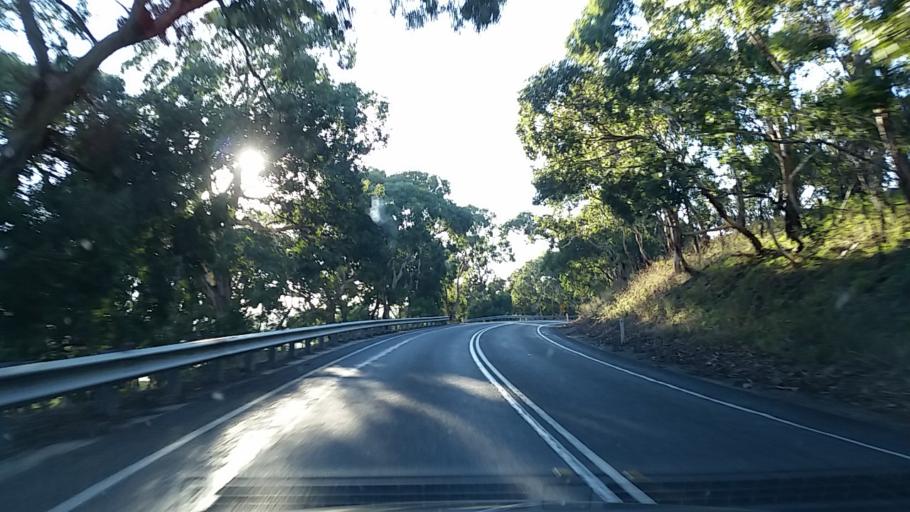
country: AU
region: South Australia
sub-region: Alexandrina
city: Goolwa
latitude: -35.3904
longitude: 138.7517
